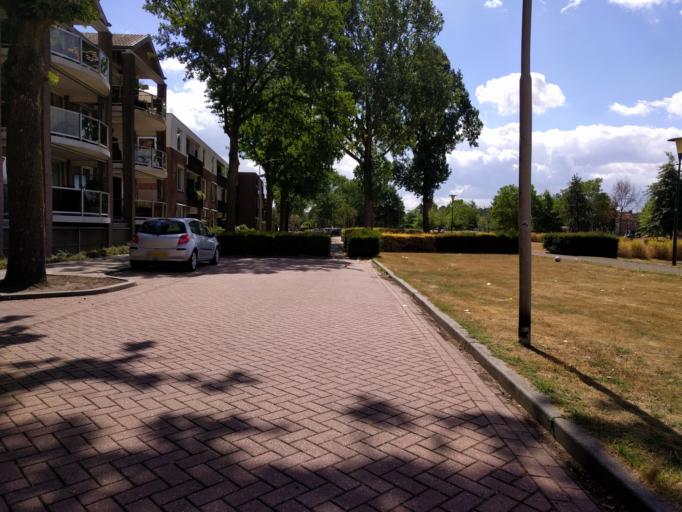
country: NL
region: Gelderland
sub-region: Gemeente Nijmegen
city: Nijmegen
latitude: 51.8412
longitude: 5.8356
